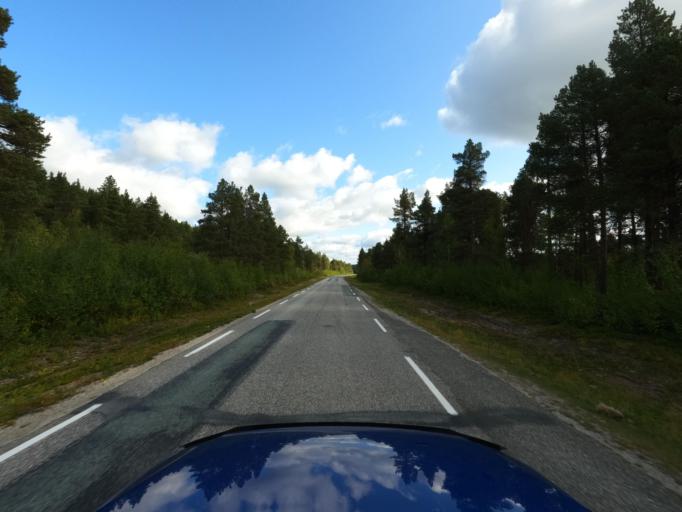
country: NO
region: Finnmark Fylke
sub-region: Karasjok
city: Karasjohka
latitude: 69.4307
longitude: 25.1218
